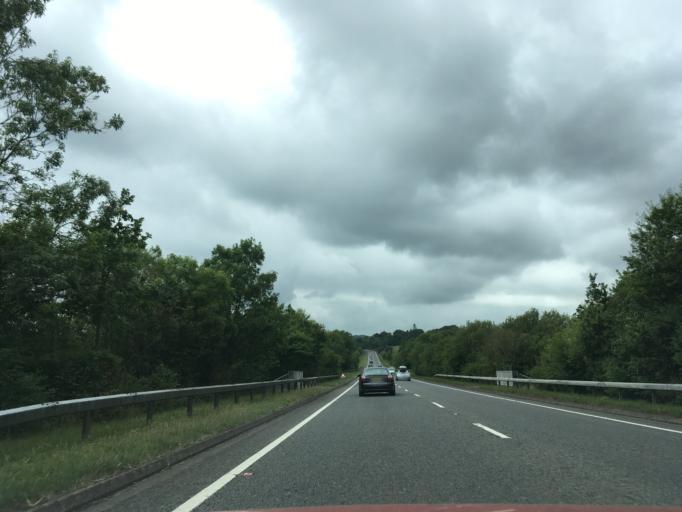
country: GB
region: Wales
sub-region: Carmarthenshire
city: Whitland
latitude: 51.8255
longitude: -4.6046
